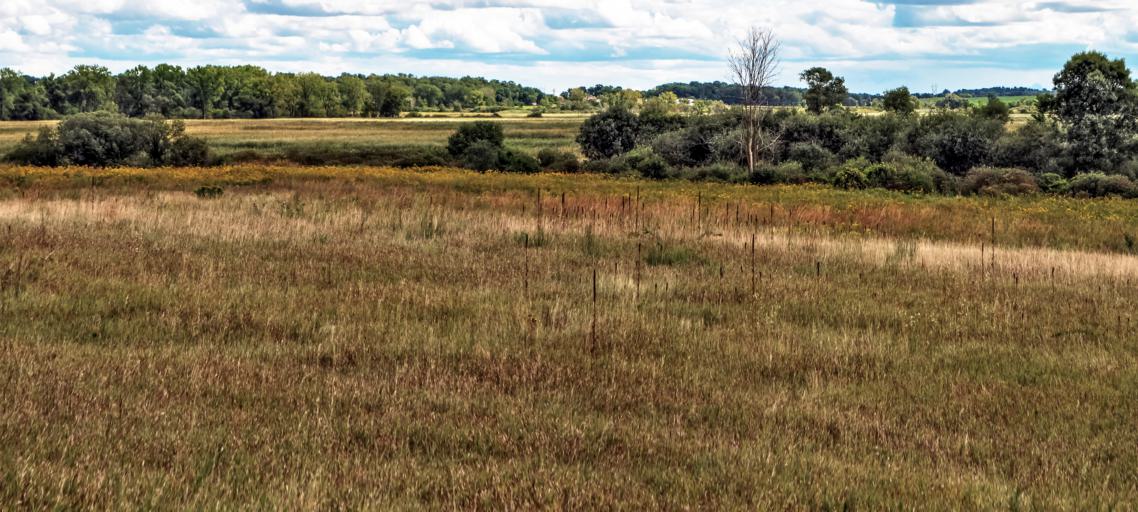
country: US
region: Wisconsin
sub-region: Jefferson County
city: Lake Mills
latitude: 43.0353
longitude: -88.9250
